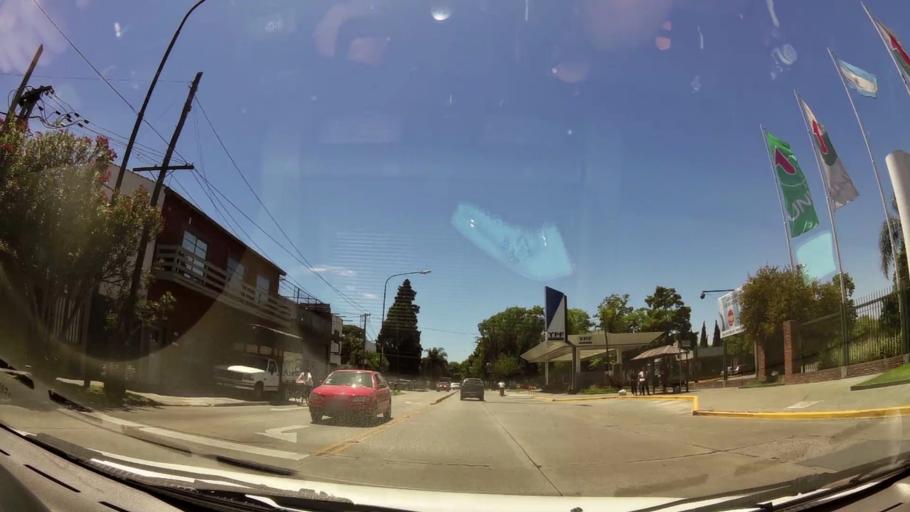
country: AR
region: Buenos Aires
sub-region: Partido de San Isidro
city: San Isidro
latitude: -34.5055
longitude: -58.5265
